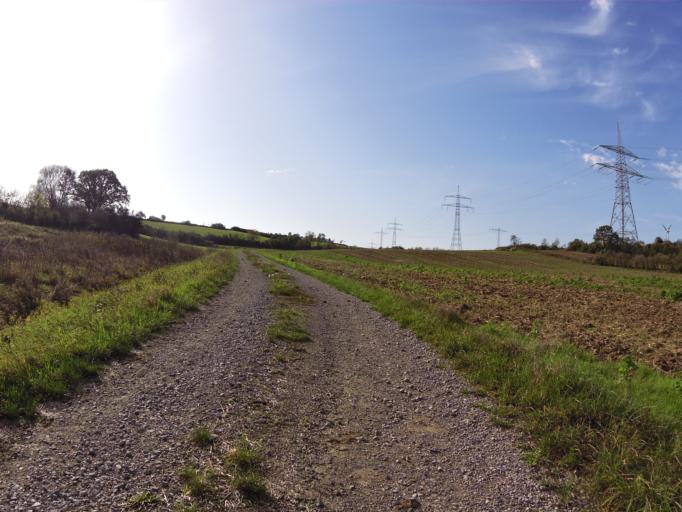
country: DE
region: Bavaria
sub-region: Regierungsbezirk Unterfranken
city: Theilheim
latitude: 49.7545
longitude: 10.0582
